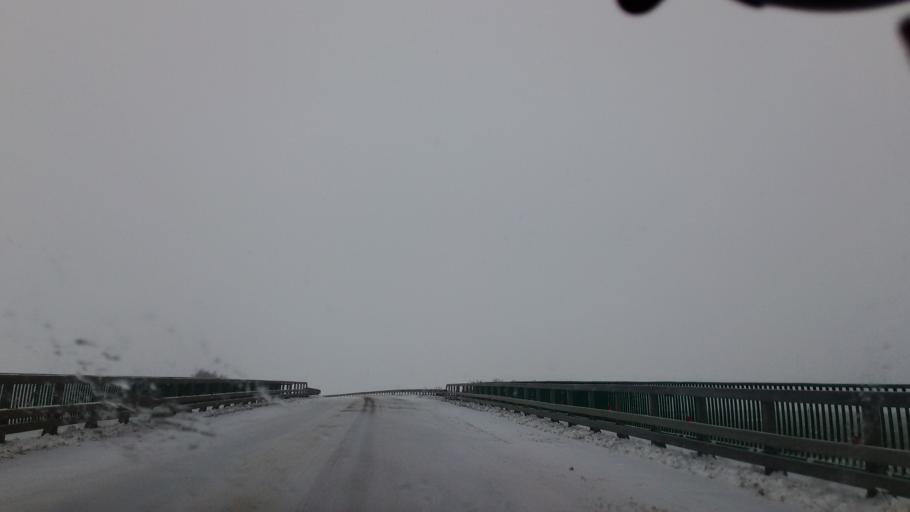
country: RU
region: Tula
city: Bogoroditsk
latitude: 53.7088
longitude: 38.0464
